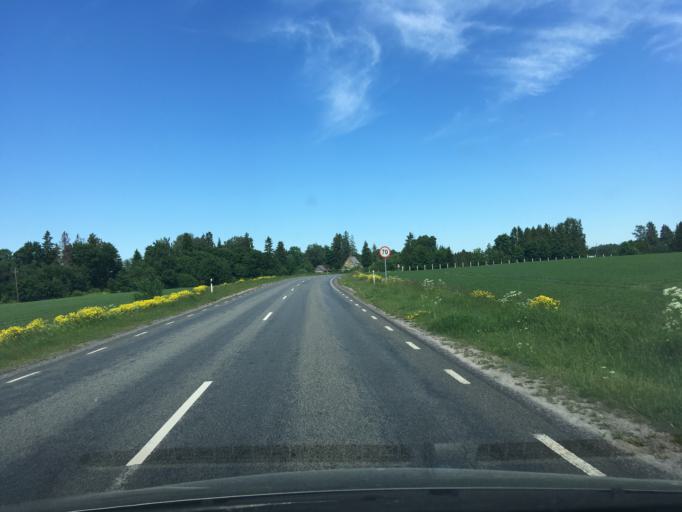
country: EE
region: Harju
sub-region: Raasiku vald
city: Raasiku
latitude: 59.1147
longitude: 25.1683
